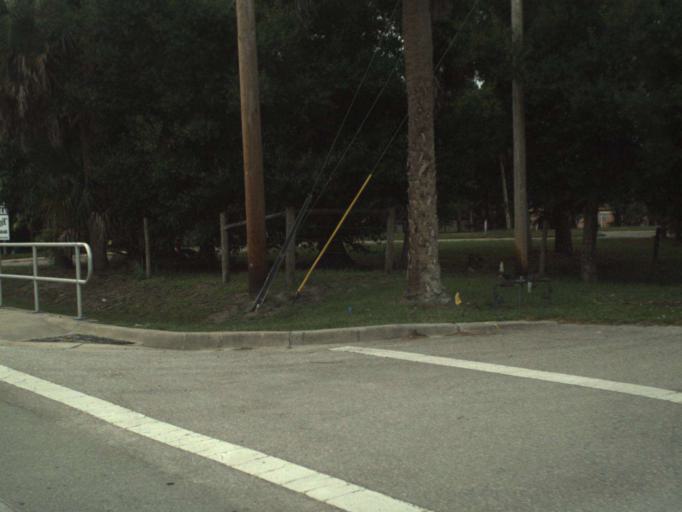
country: US
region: Florida
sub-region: Saint Lucie County
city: White City
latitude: 27.3848
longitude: -80.3504
